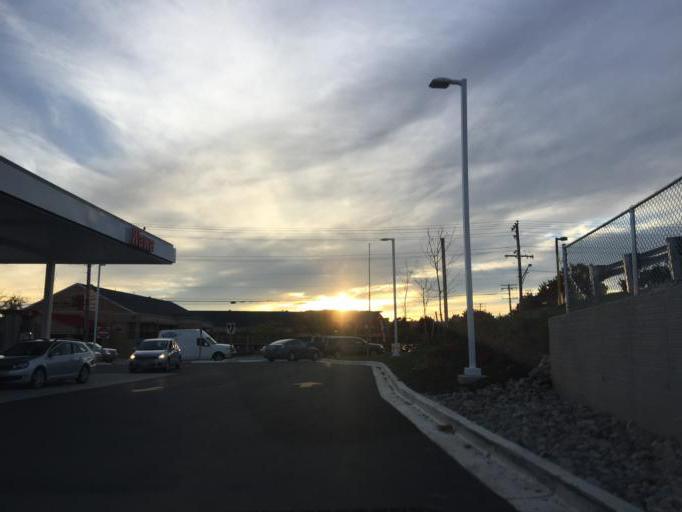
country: US
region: Maryland
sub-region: Baltimore County
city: Cockeysville
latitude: 39.4662
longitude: -76.6367
